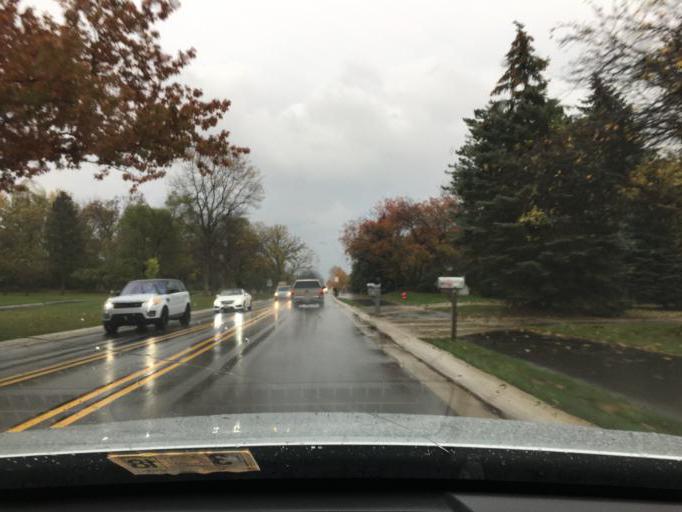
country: US
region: Michigan
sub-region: Oakland County
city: Auburn Hills
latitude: 42.6942
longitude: -83.1934
